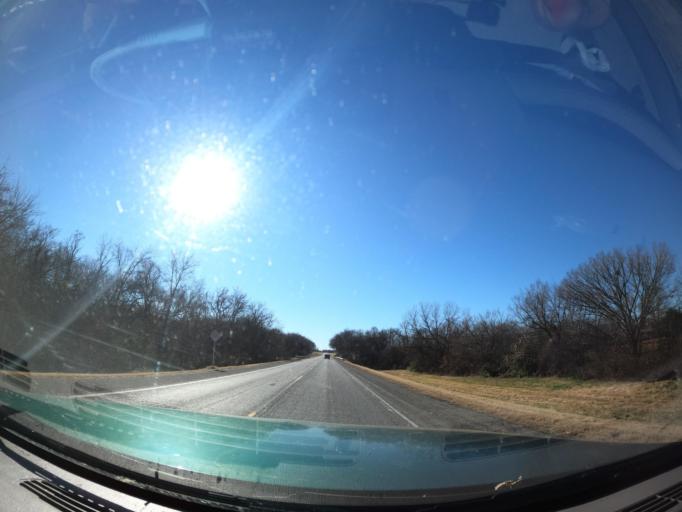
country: US
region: Oklahoma
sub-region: Muskogee County
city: Haskell
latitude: 35.8729
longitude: -95.6668
